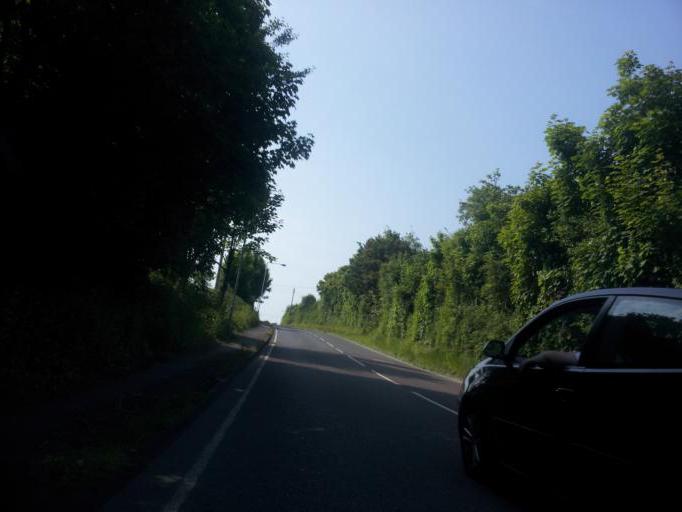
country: GB
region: England
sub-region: Kent
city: Aylesford
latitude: 51.3345
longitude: 0.4771
